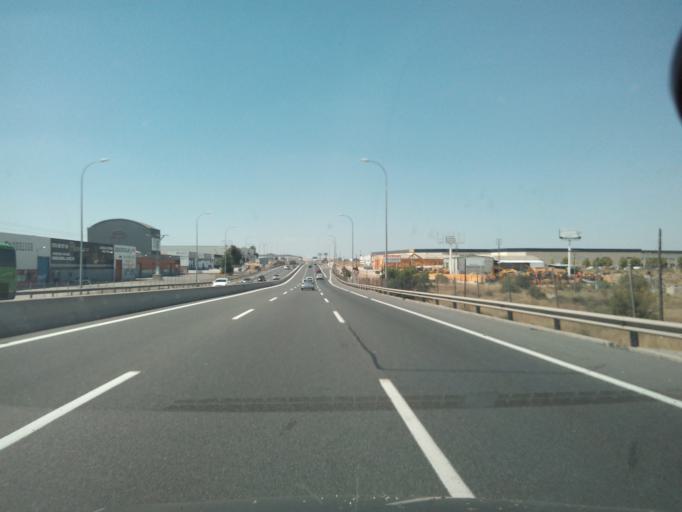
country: ES
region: Castille-La Mancha
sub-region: Province of Toledo
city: Sesena
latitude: 40.1122
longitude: -3.6499
